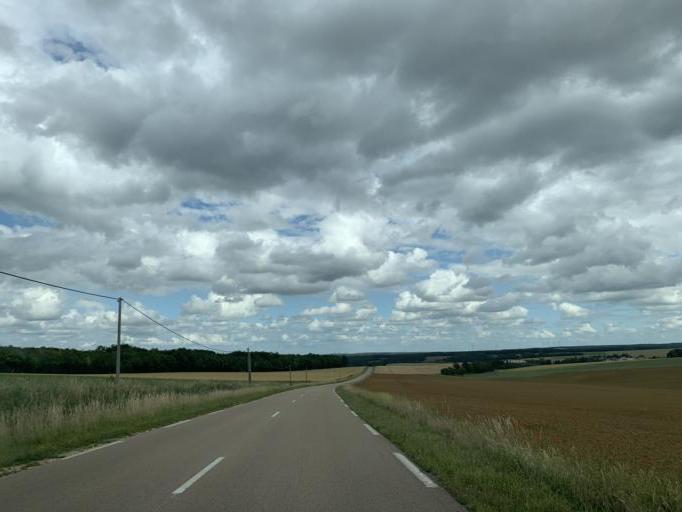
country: FR
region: Bourgogne
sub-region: Departement de l'Yonne
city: Vermenton
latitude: 47.7382
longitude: 3.7664
